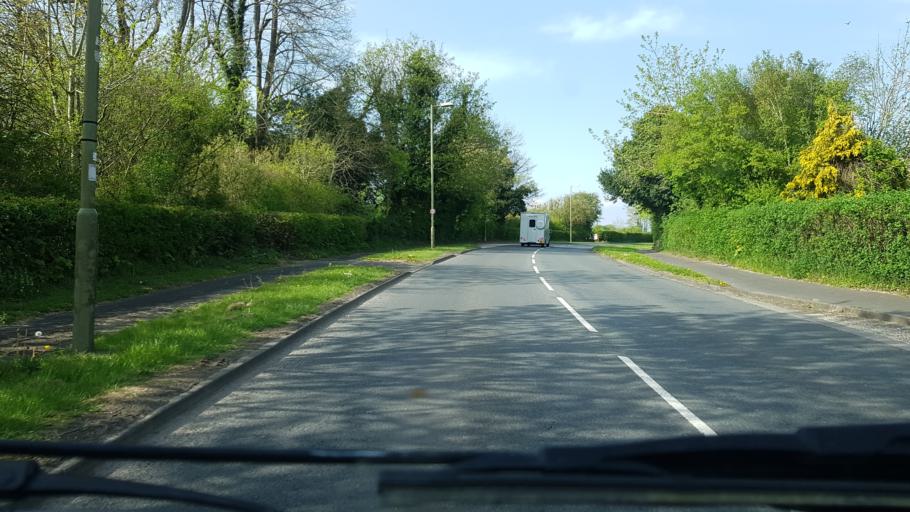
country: GB
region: England
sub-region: Hampshire
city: Basingstoke
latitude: 51.2634
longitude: -1.1378
